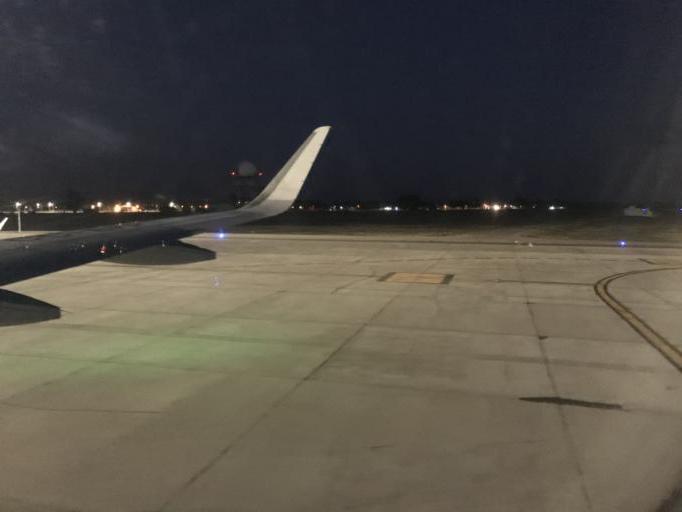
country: AR
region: Mendoza
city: Las Heras
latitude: -32.8272
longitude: -68.7971
